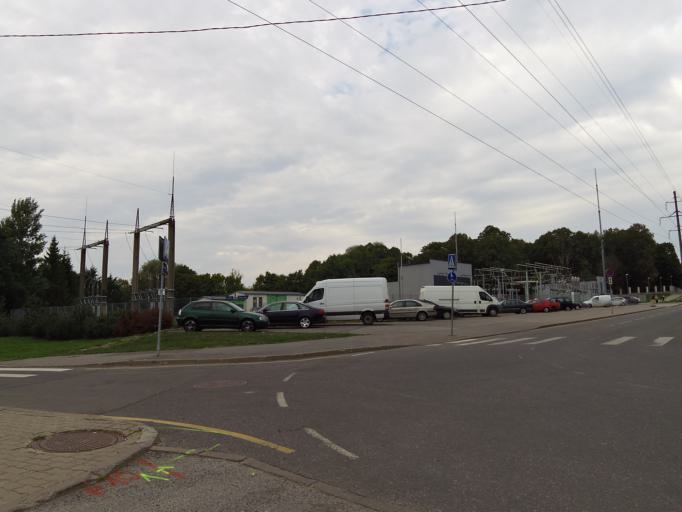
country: EE
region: Harju
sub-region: Tallinna linn
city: Tallinn
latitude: 59.4503
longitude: 24.6841
